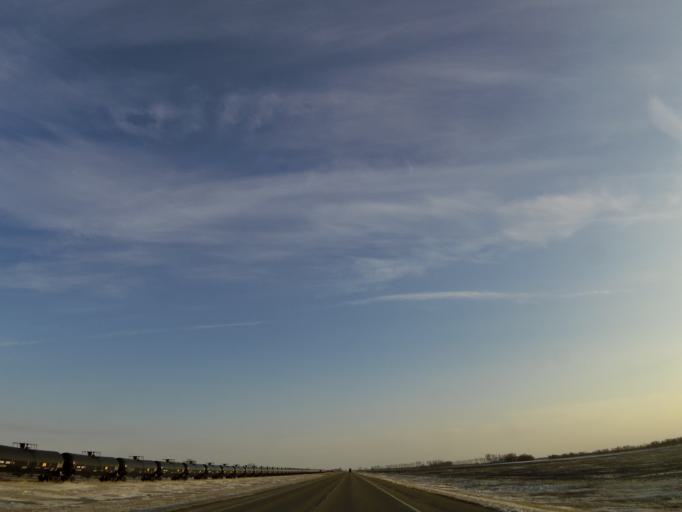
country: US
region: North Dakota
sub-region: Walsh County
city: Grafton
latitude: 48.4955
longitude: -97.4344
